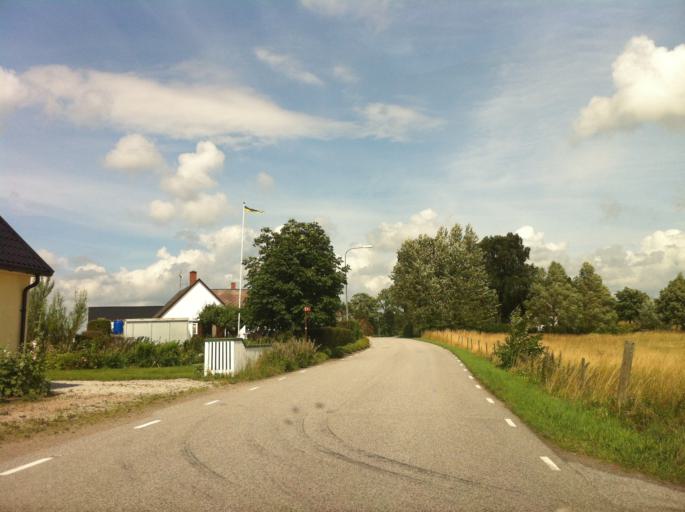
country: SE
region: Skane
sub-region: Skurups Kommun
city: Skurup
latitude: 55.4570
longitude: 13.4289
